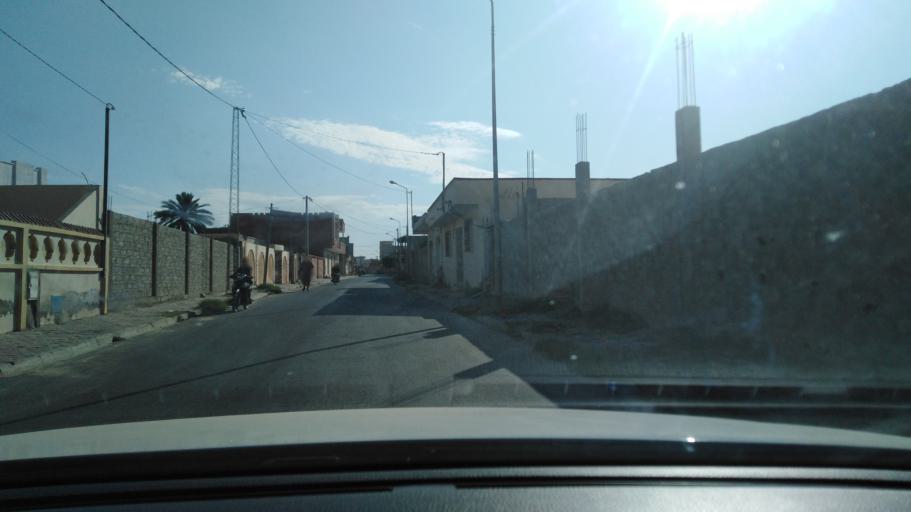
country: TN
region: Qabis
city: Gabes
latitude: 33.9413
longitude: 10.0743
